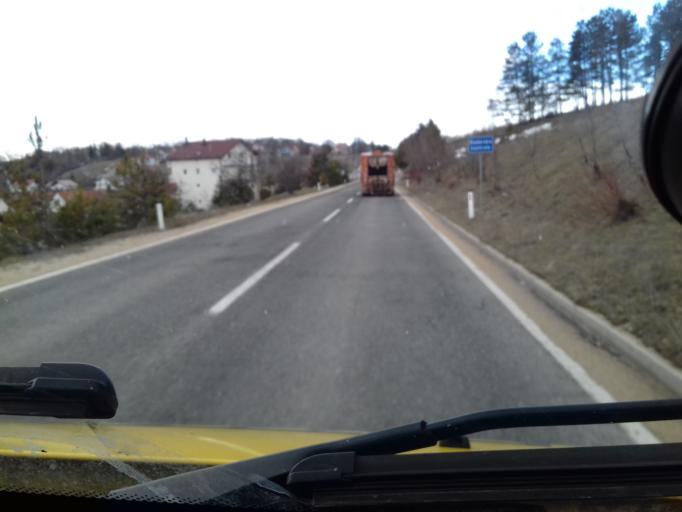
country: BA
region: Federation of Bosnia and Herzegovina
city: Tomislavgrad
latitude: 43.7265
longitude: 17.2243
